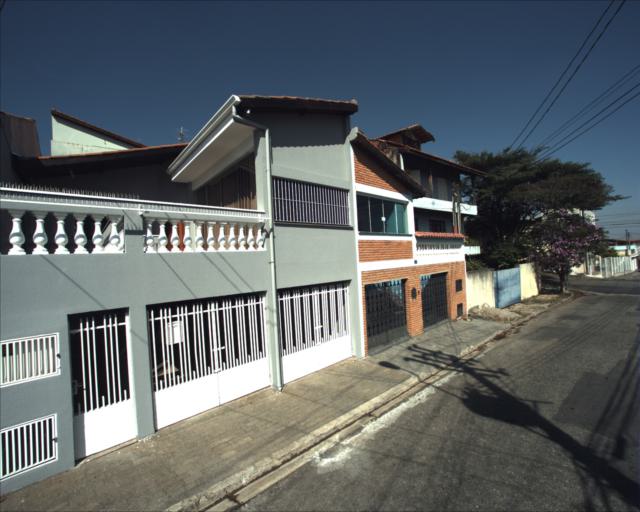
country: BR
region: Sao Paulo
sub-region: Sorocaba
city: Sorocaba
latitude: -23.4668
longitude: -47.4347
